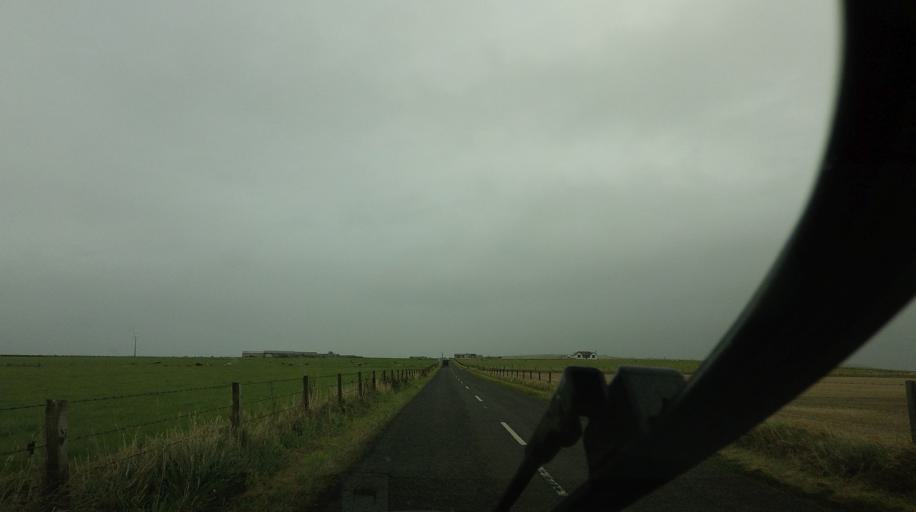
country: GB
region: Scotland
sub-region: Orkney Islands
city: Stromness
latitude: 59.1308
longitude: -3.3093
